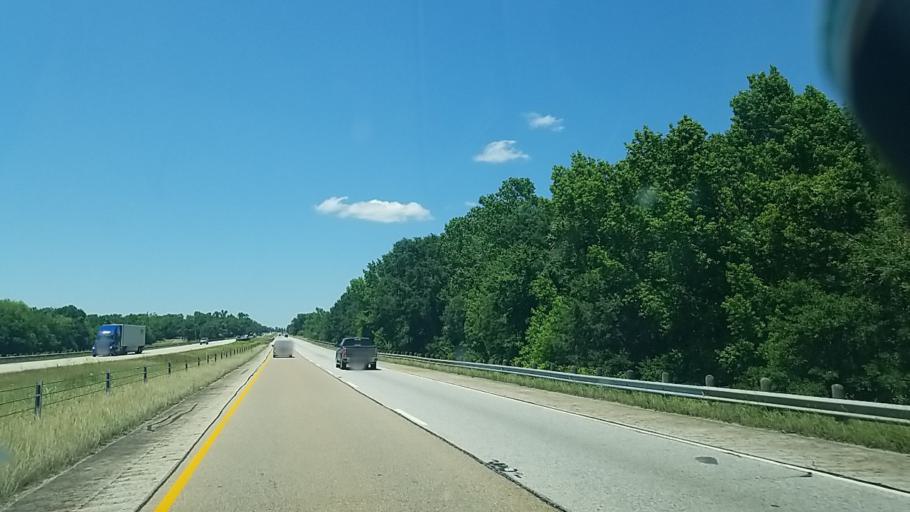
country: US
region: Texas
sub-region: Leon County
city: Centerville
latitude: 31.1862
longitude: -95.9914
